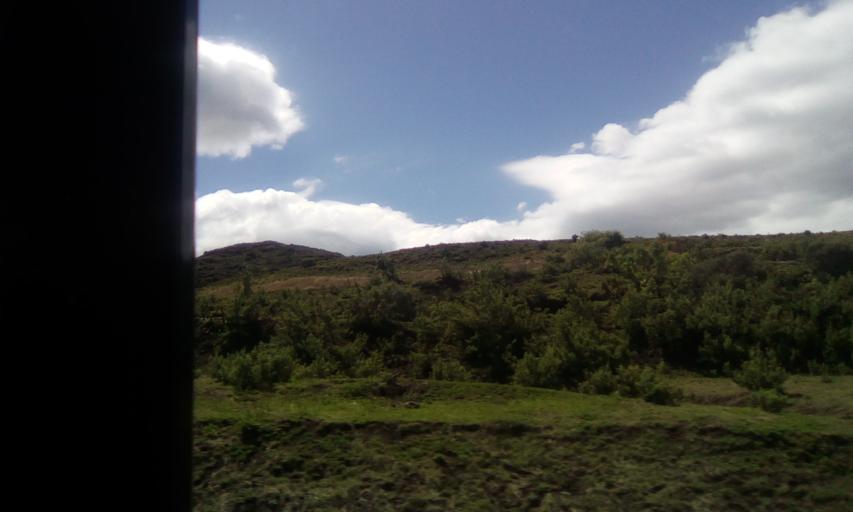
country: LS
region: Maseru
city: Nako
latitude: -29.6570
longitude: 27.8087
